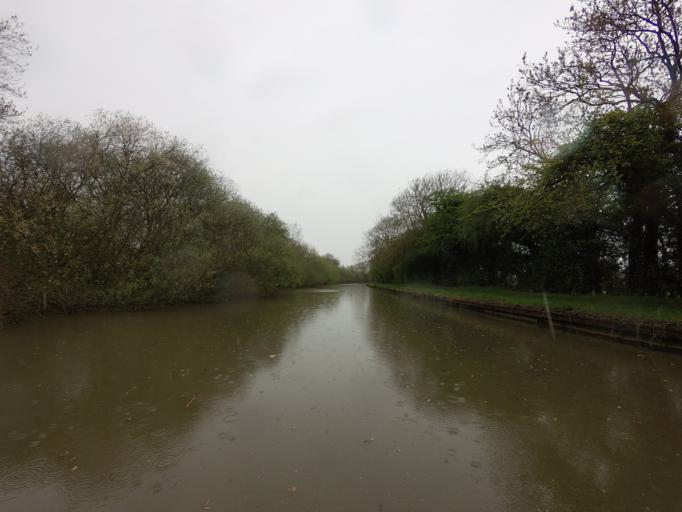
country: GB
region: England
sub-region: Milton Keynes
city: Castlethorpe
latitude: 52.0883
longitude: -0.8603
